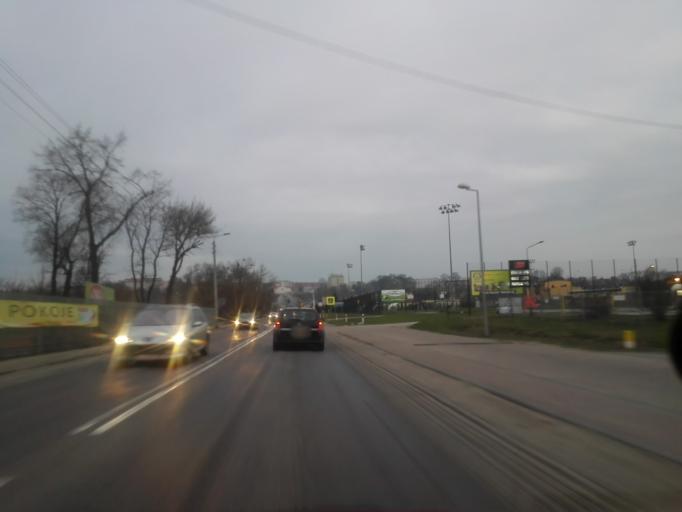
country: PL
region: Podlasie
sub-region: Powiat lomzynski
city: Piatnica
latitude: 53.1864
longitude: 22.0861
